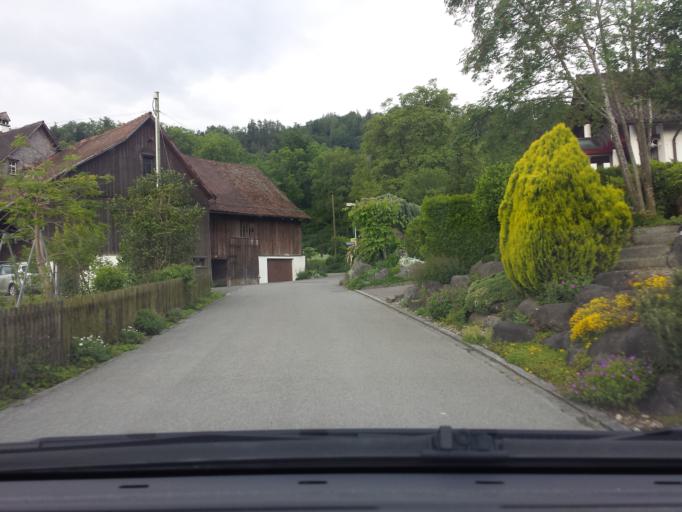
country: CH
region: Appenzell Innerrhoden
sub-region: Appenzell Inner Rhodes
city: Balgach
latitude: 47.4241
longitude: 9.6060
